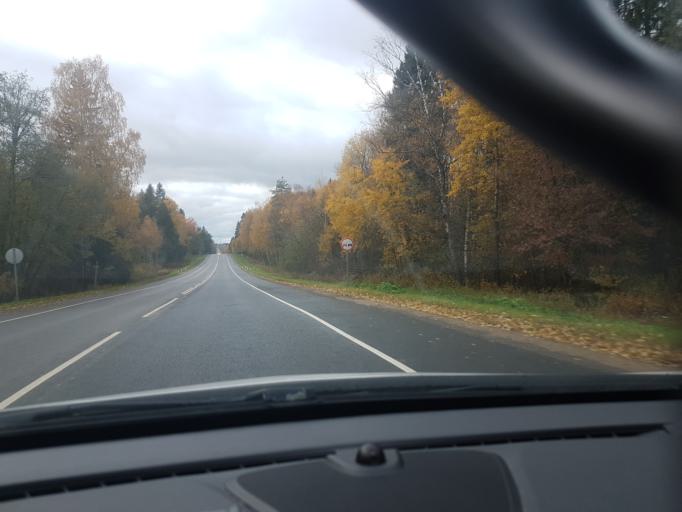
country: RU
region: Moskovskaya
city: Sychevo
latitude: 56.0061
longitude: 36.2641
